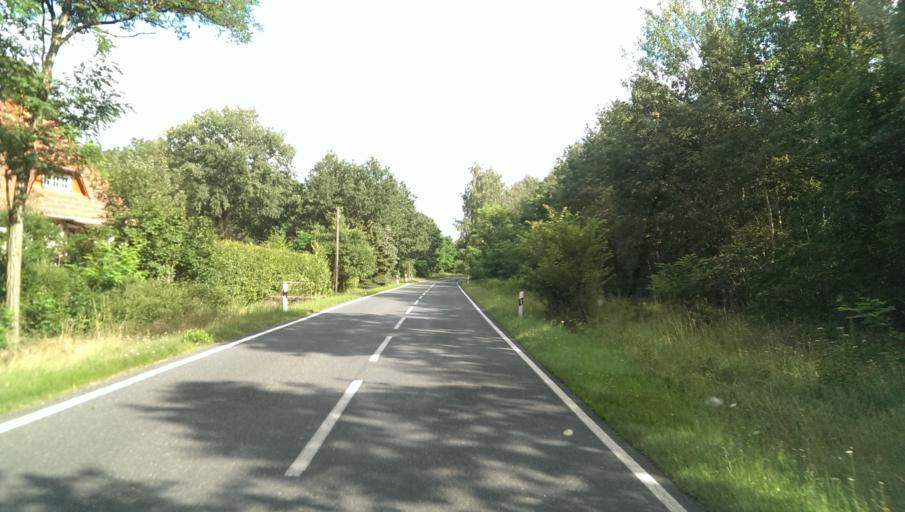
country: DE
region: Saxony-Anhalt
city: Radis
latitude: 51.7598
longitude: 12.5042
